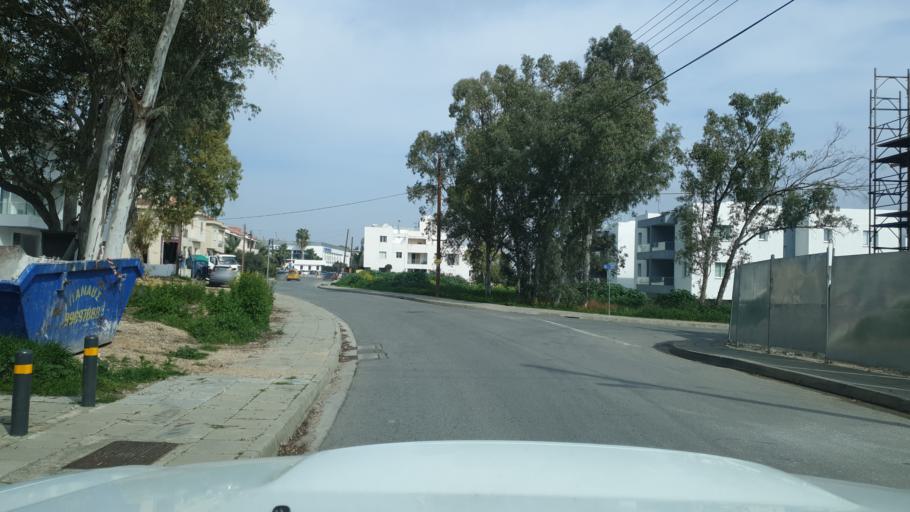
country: CY
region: Lefkosia
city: Nicosia
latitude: 35.1460
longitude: 33.3211
